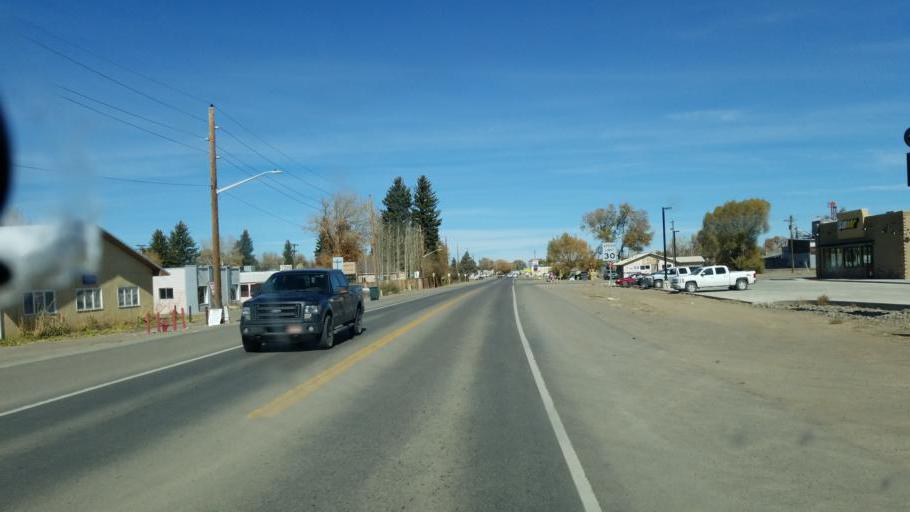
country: US
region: Colorado
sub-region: Conejos County
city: Conejos
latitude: 37.2721
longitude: -105.9626
